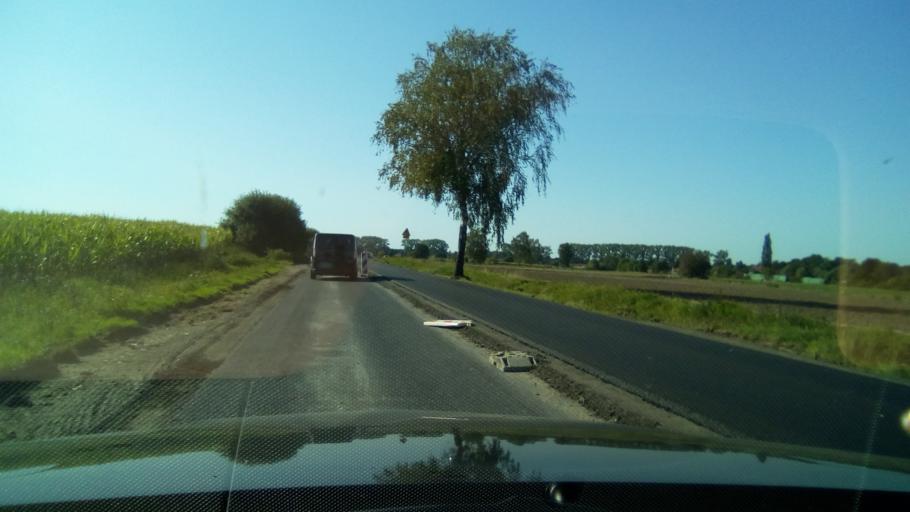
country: PL
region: West Pomeranian Voivodeship
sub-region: Powiat gryficki
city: Ploty
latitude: 53.8131
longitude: 15.1779
